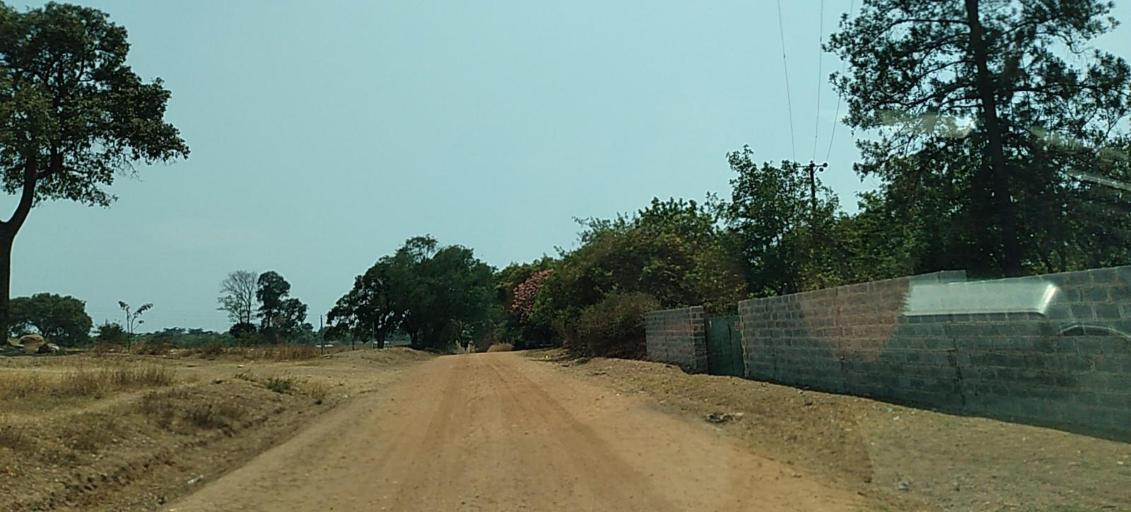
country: ZM
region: Copperbelt
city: Chingola
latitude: -12.6247
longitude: 27.9416
